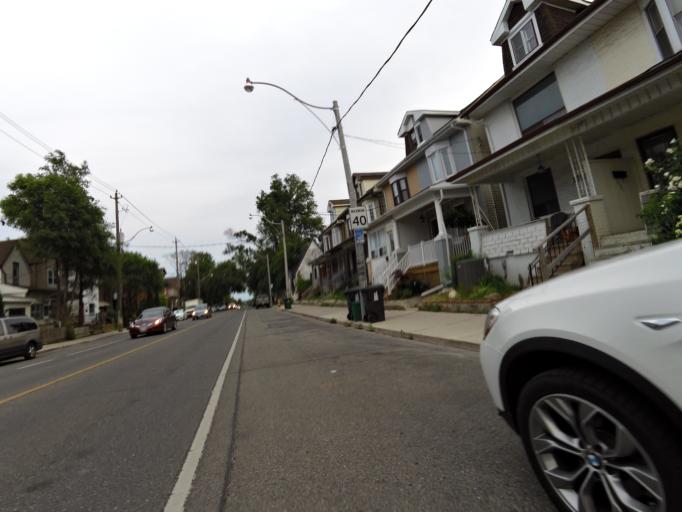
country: CA
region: Ontario
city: Toronto
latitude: 43.6765
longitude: -79.3388
